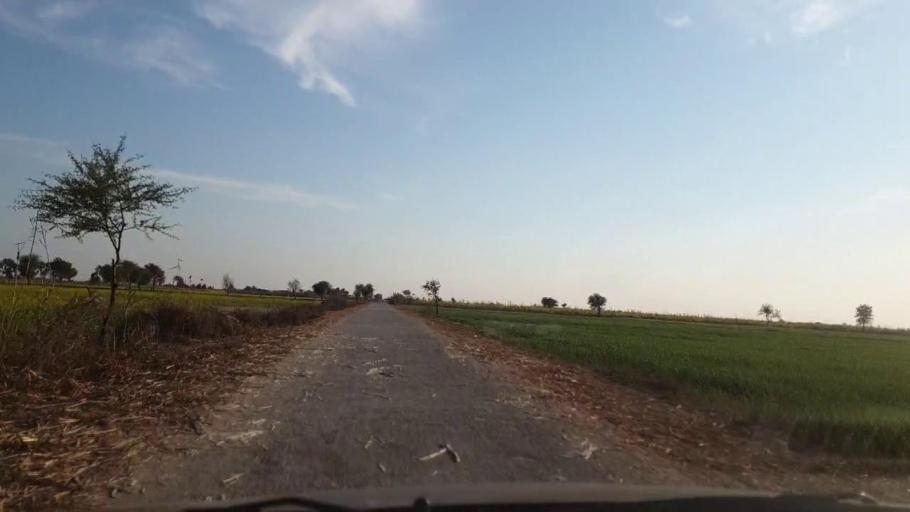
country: PK
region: Sindh
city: Khadro
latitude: 26.1779
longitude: 68.7527
